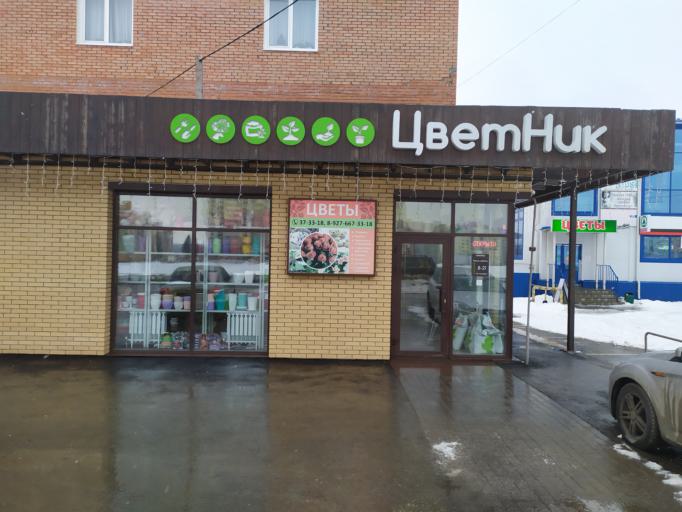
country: RU
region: Chuvashia
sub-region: Cheboksarskiy Rayon
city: Cheboksary
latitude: 56.1160
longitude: 47.2228
